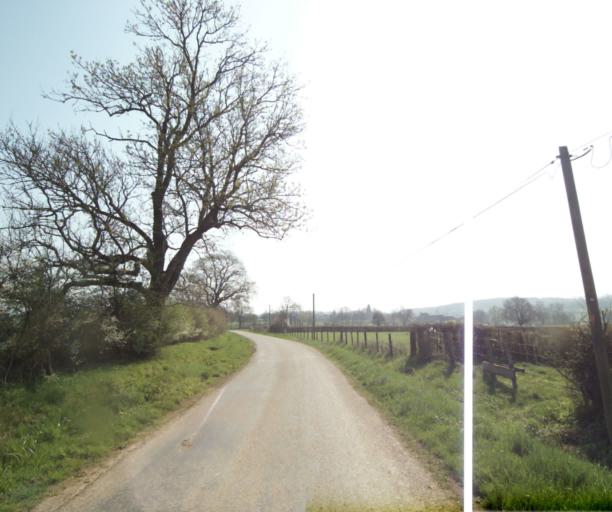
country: FR
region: Bourgogne
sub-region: Departement de Saone-et-Loire
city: Charolles
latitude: 46.4760
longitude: 4.3265
